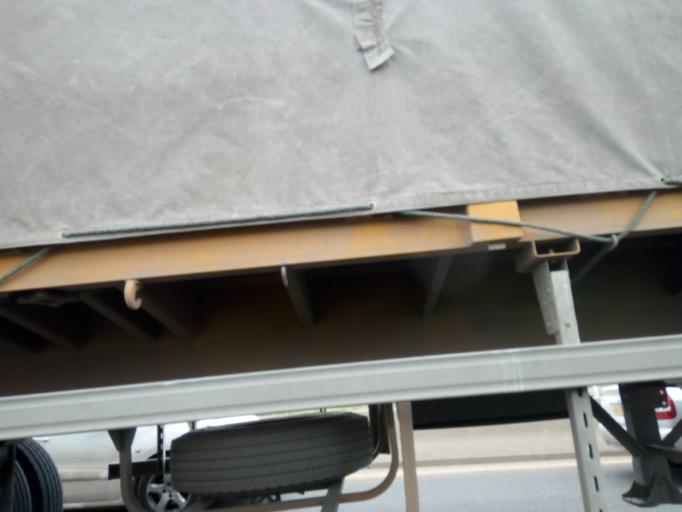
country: DZ
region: Bordj Bou Arreridj
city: Bordj Bou Arreridj
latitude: 36.0960
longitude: 4.7579
